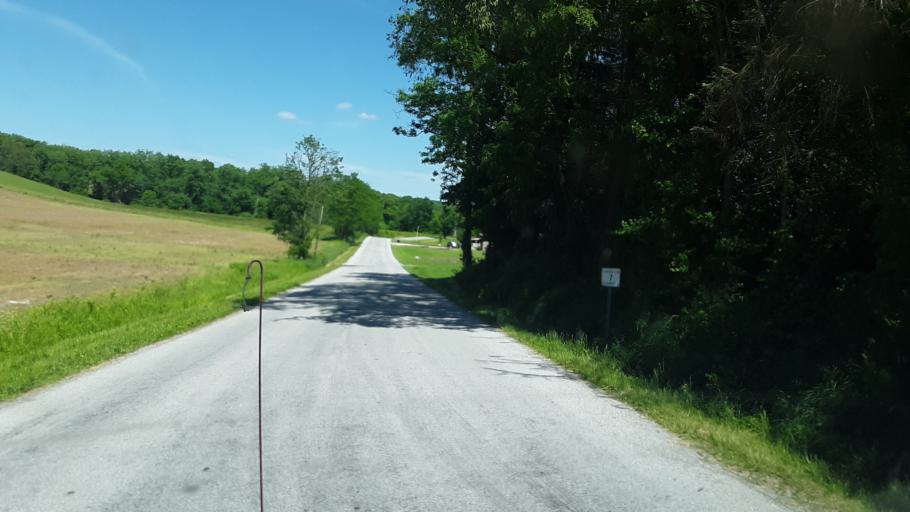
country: US
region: Ohio
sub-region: Coshocton County
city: Coshocton
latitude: 40.2302
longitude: -81.8342
